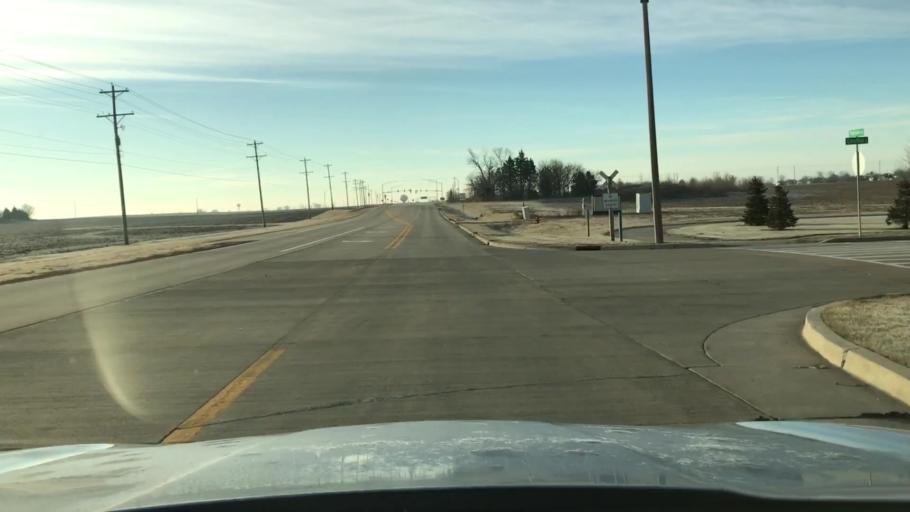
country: US
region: Illinois
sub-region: McLean County
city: Normal
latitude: 40.5516
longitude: -88.9444
